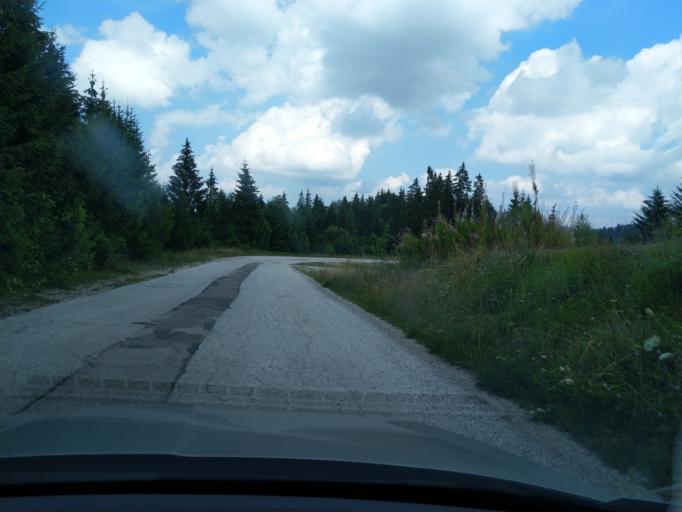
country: RS
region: Central Serbia
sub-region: Zlatiborski Okrug
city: Nova Varos
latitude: 43.5320
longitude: 19.8950
